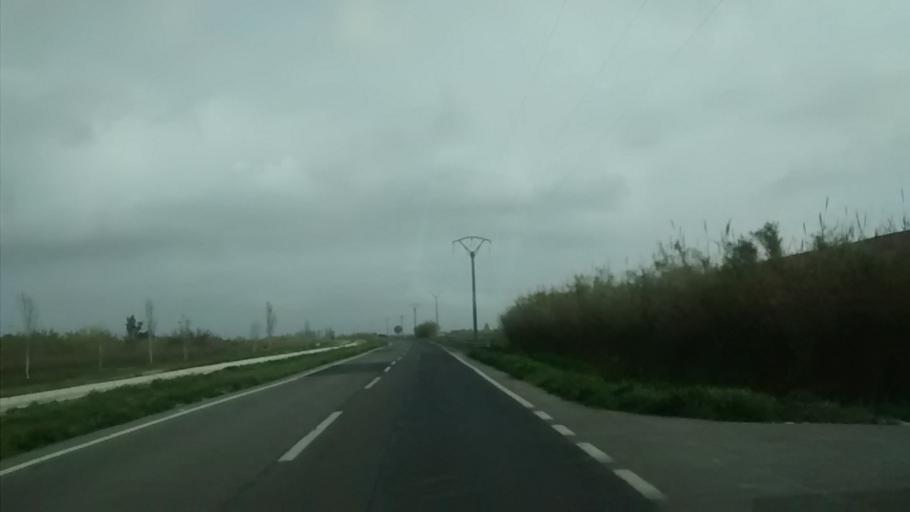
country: ES
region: Catalonia
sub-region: Provincia de Tarragona
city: Sant Carles de la Rapita
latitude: 40.6301
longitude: 0.6010
